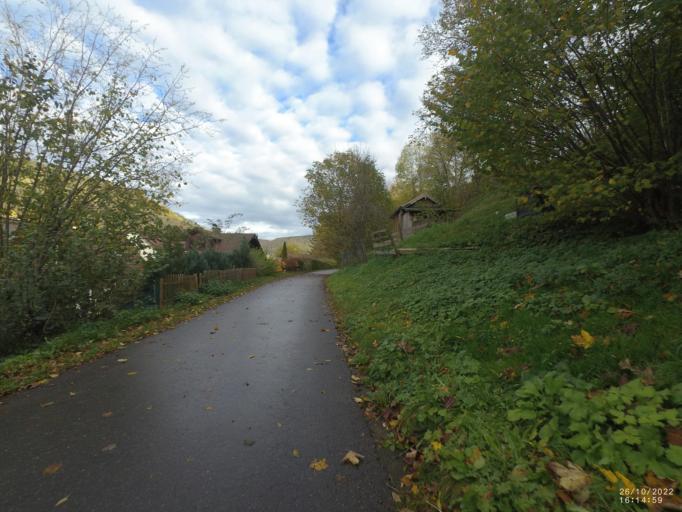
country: DE
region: Baden-Wuerttemberg
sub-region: Regierungsbezirk Stuttgart
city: Donzdorf
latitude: 48.7089
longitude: 9.8623
